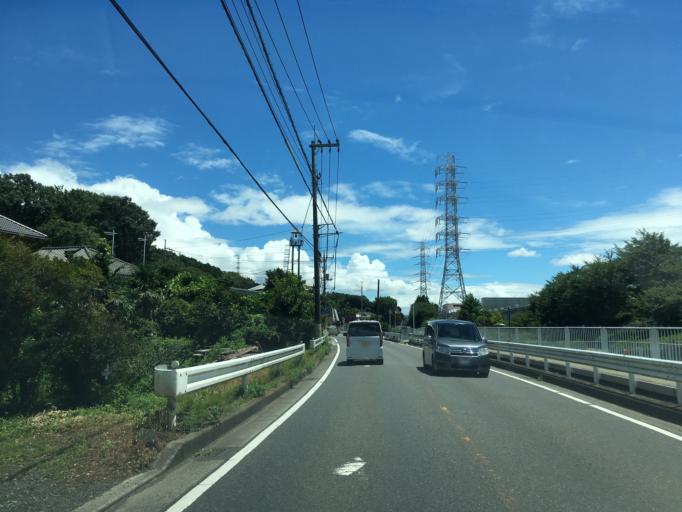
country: JP
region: Tokyo
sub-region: Machida-shi
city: Machida
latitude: 35.5460
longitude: 139.4924
